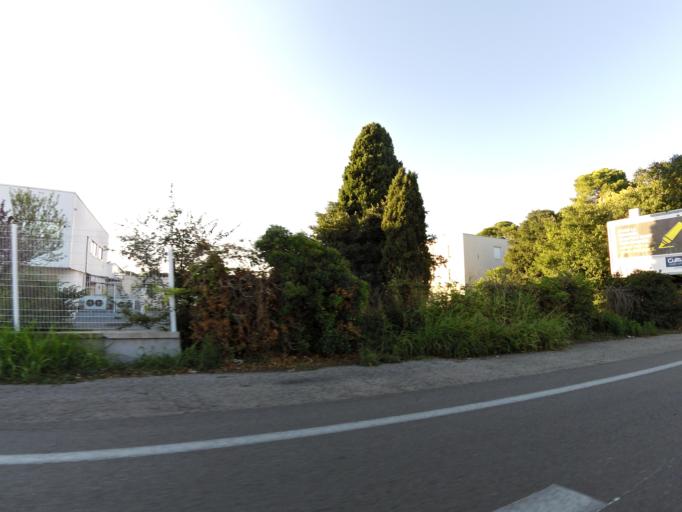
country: FR
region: Languedoc-Roussillon
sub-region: Departement du Gard
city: Milhaud
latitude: 43.8083
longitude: 4.3262
